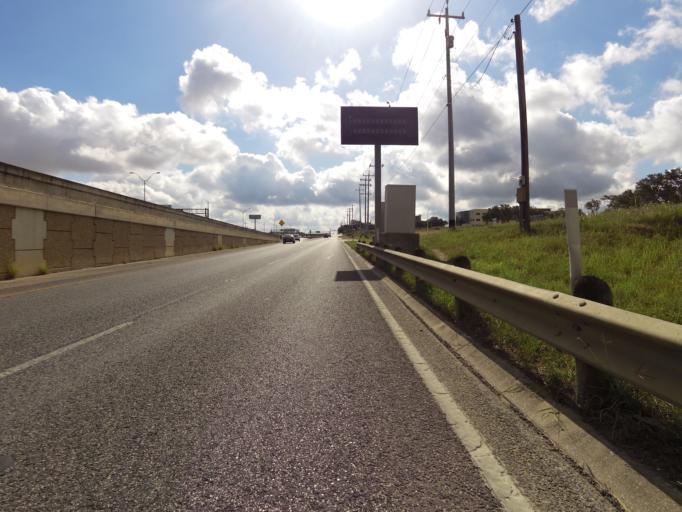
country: US
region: Texas
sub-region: Bexar County
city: Shavano Park
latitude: 29.5909
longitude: -98.5947
